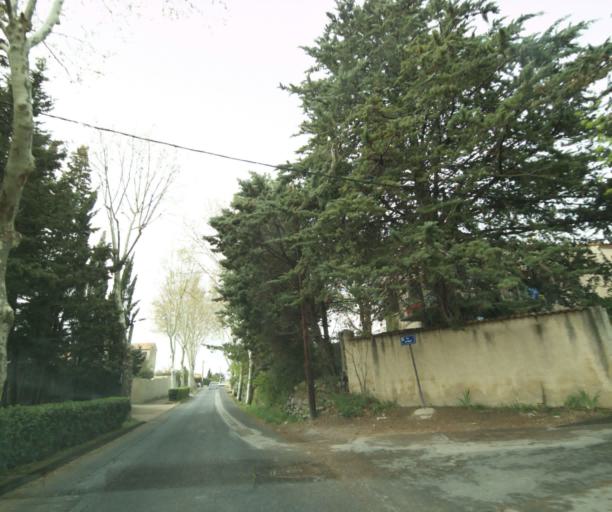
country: FR
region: Languedoc-Roussillon
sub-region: Departement de l'Herault
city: Fabregues
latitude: 43.5526
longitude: 3.7718
